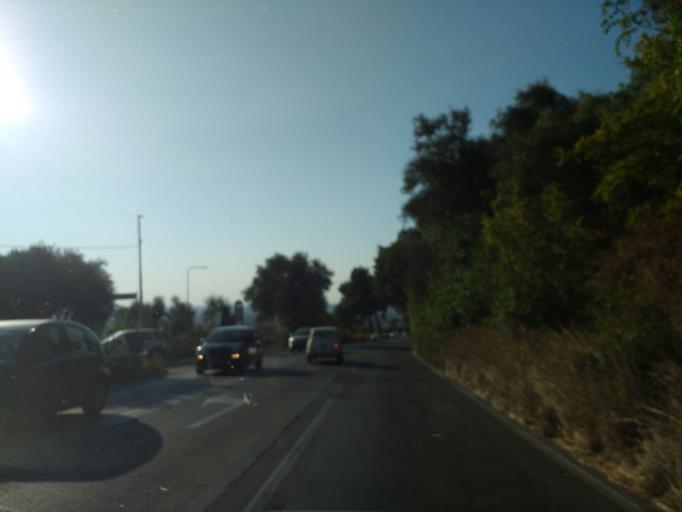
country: IT
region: Latium
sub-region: Citta metropolitana di Roma Capitale
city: Tivoli
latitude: 41.9492
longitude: 12.7898
